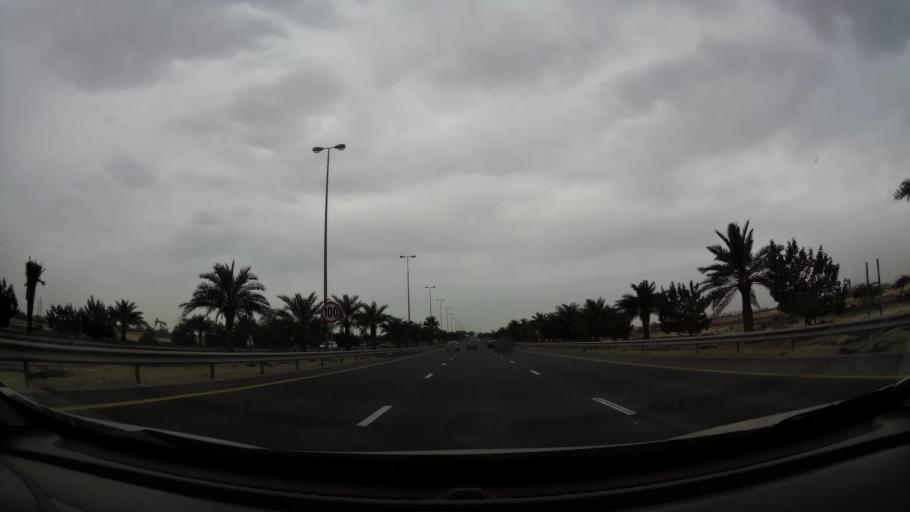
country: BH
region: Central Governorate
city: Dar Kulayb
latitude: 26.0850
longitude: 50.5395
